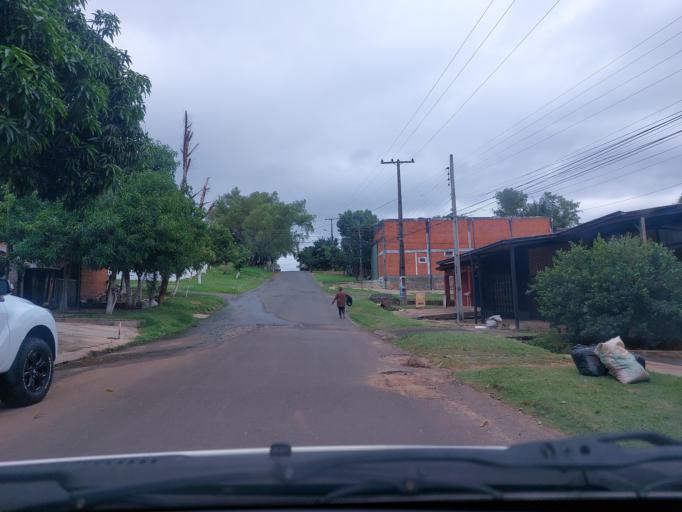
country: PY
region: San Pedro
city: Guayaybi
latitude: -24.6623
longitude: -56.4387
